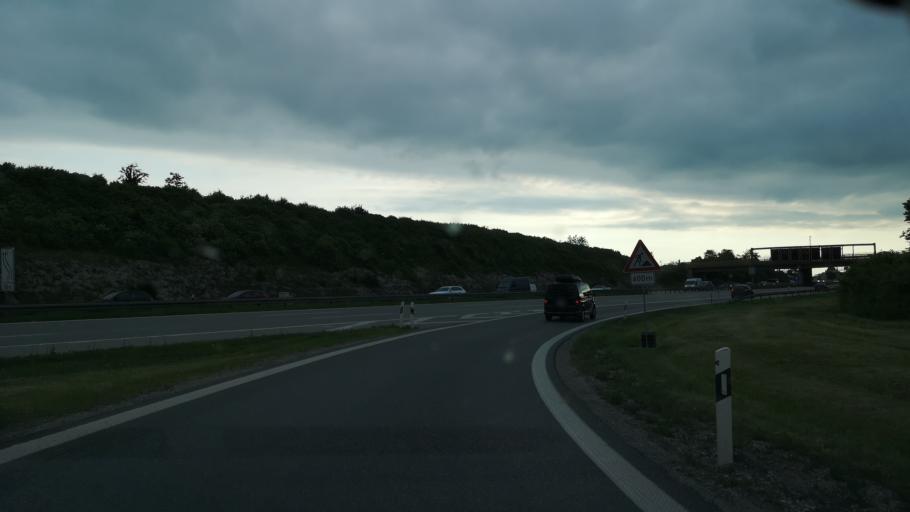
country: DE
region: Bavaria
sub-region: Upper Bavaria
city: Feldkirchen
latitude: 48.1428
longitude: 11.7421
